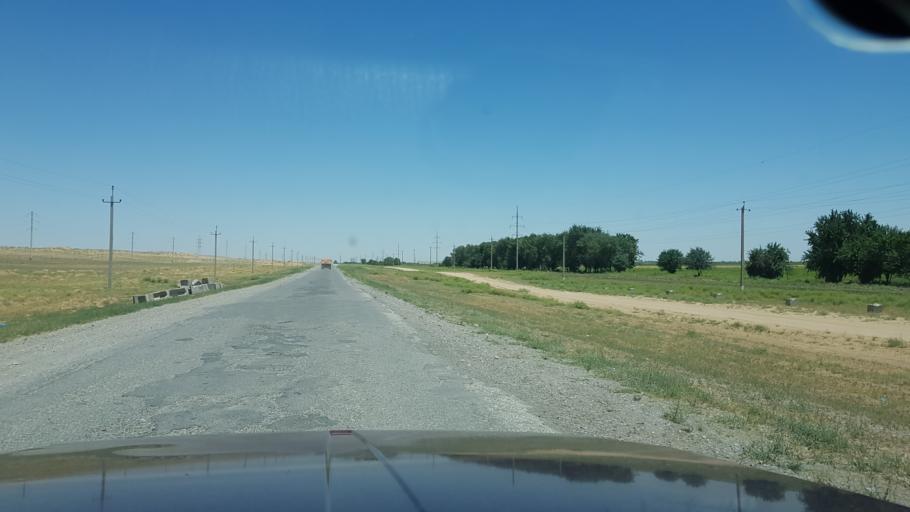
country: TM
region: Ahal
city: Annau
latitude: 37.8690
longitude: 58.7171
